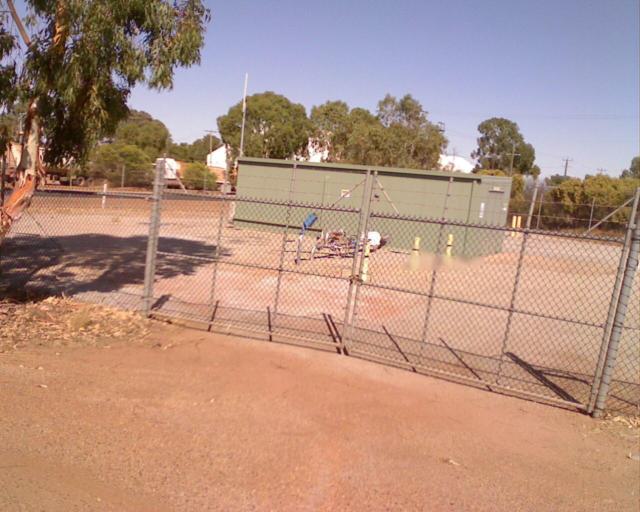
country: AU
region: Western Australia
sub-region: Wongan-Ballidu
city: Wongan Hills
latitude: -30.5992
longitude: 116.7743
